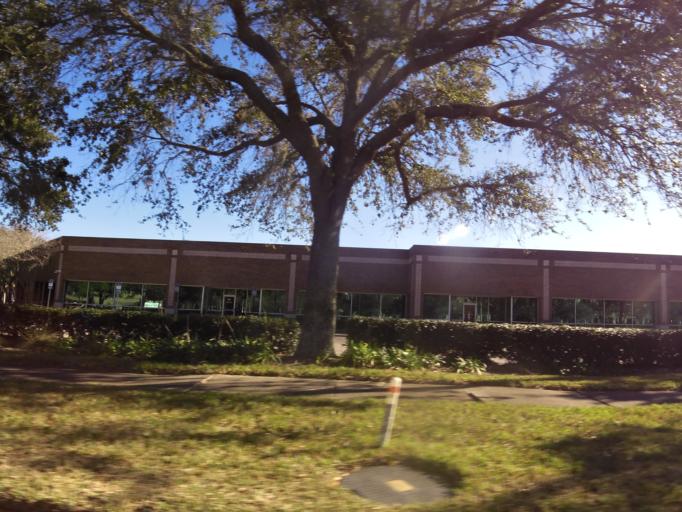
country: US
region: Florida
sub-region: Duval County
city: Jacksonville
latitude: 30.2478
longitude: -81.5823
